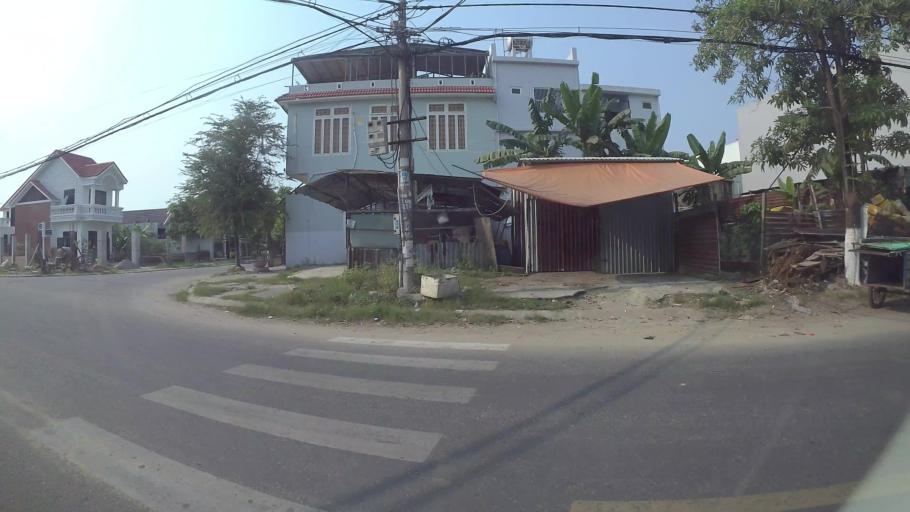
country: VN
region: Da Nang
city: Lien Chieu
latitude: 16.0488
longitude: 108.1716
